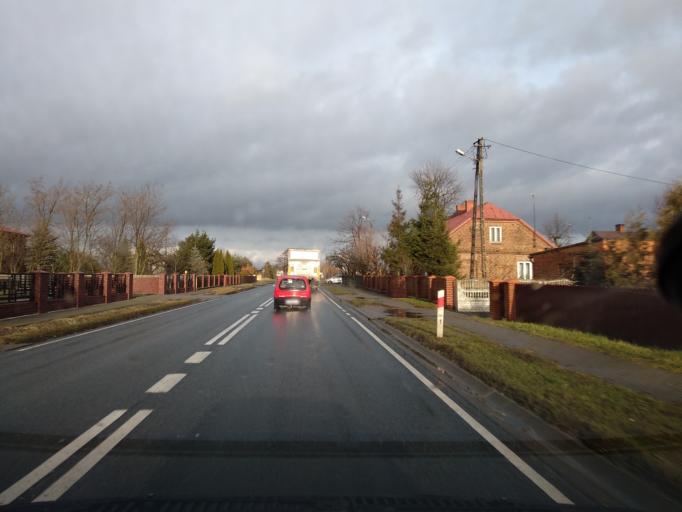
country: PL
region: Greater Poland Voivodeship
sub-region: Powiat koninski
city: Rychwal
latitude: 52.1171
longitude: 18.1678
